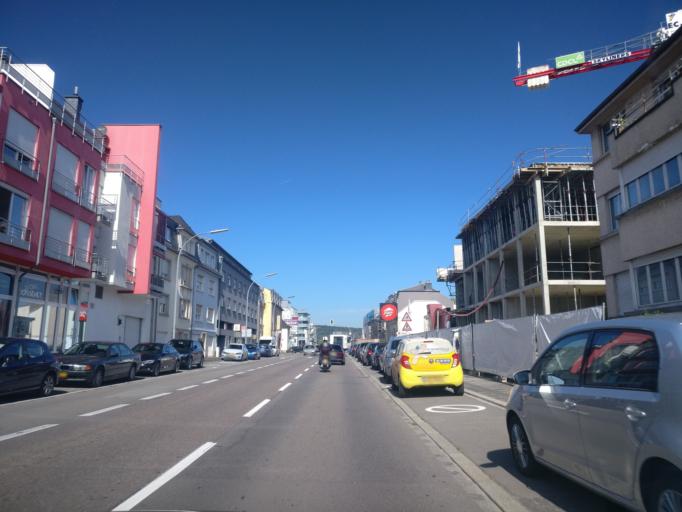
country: LU
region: Luxembourg
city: Bereldange
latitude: 49.6444
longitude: 6.1291
